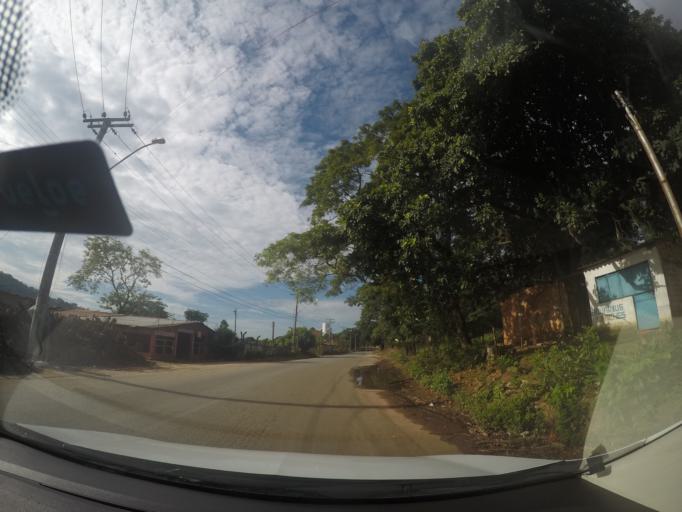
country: BR
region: Goias
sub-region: Goiania
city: Goiania
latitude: -16.6762
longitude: -49.1999
